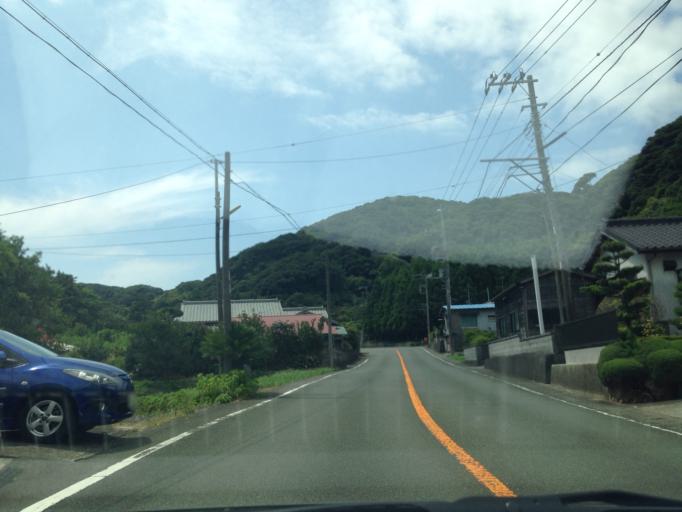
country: JP
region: Shizuoka
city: Shimoda
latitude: 34.6509
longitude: 138.8023
